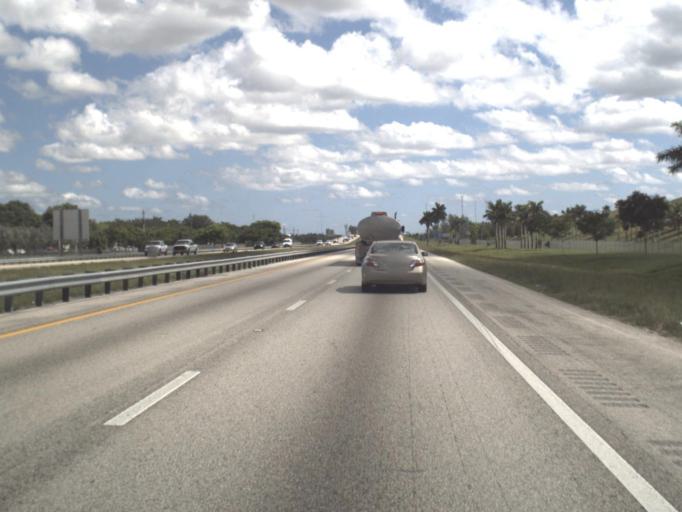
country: US
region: Florida
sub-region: Miami-Dade County
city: Country Club
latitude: 25.9710
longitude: -80.2869
